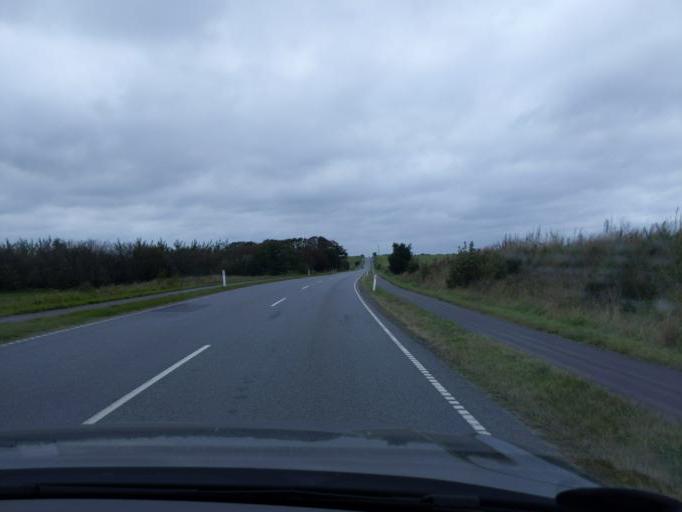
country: DK
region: North Denmark
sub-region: Mariagerfjord Kommune
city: Hobro
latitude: 56.5969
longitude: 9.7870
